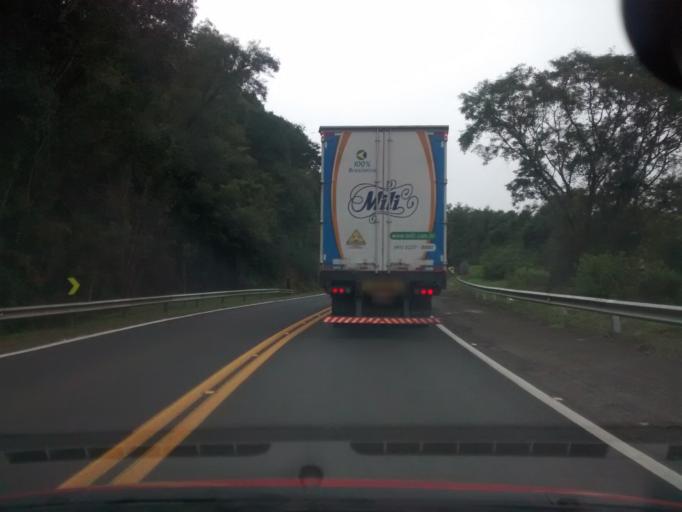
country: BR
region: Rio Grande do Sul
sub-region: Vacaria
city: Estrela
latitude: -28.1982
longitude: -50.7285
